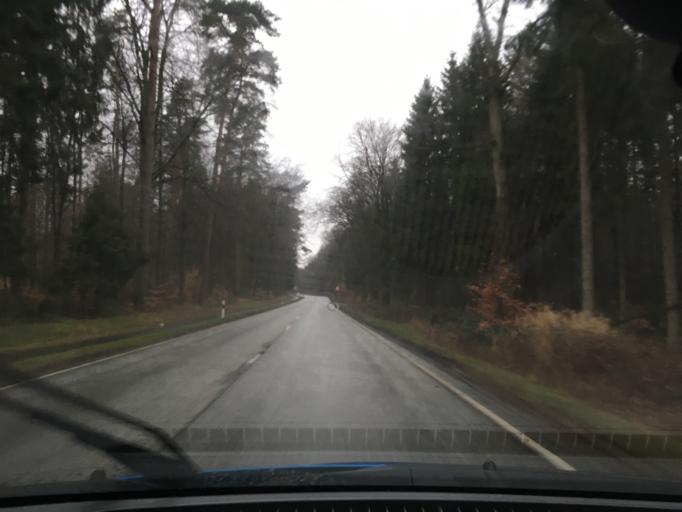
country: DE
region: Schleswig-Holstein
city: Krukow
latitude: 53.3943
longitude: 10.4768
